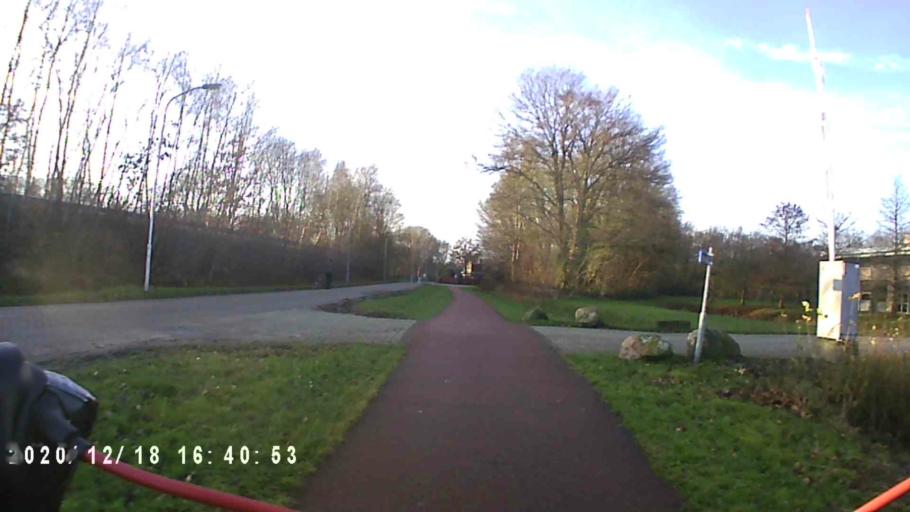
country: NL
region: Drenthe
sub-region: Gemeente Tynaarlo
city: Zuidlaren
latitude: 53.0802
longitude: 6.6708
